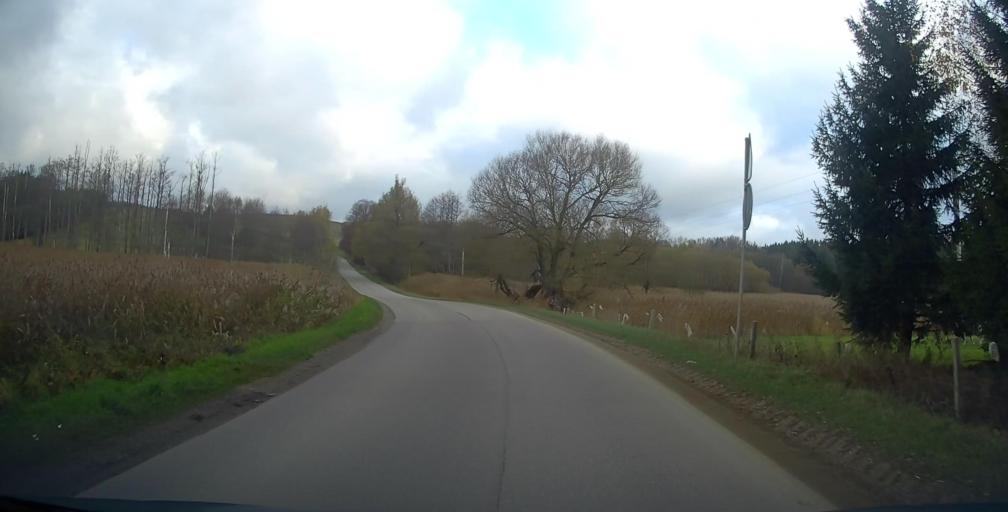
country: PL
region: Podlasie
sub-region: Suwalki
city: Suwalki
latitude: 54.2779
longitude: 22.9100
